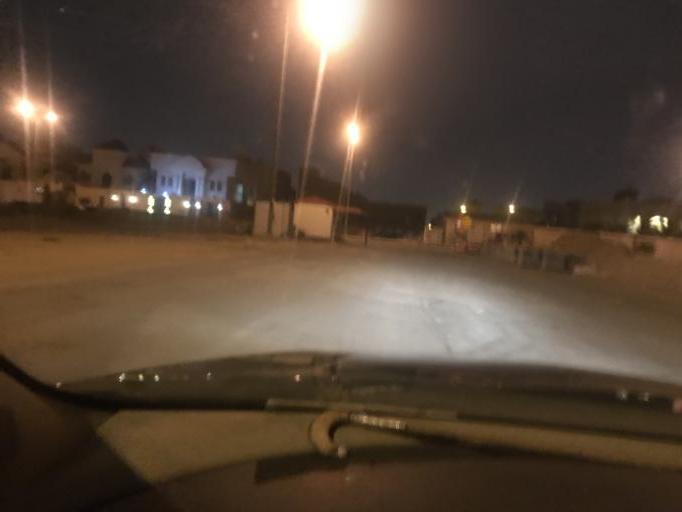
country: SA
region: Ar Riyad
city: Riyadh
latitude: 24.8056
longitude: 46.6782
